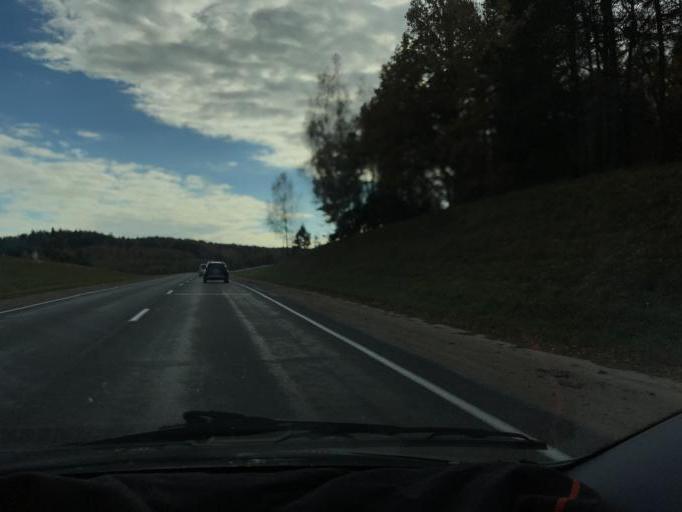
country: BY
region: Minsk
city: Lahoysk
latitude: 54.2240
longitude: 27.8334
